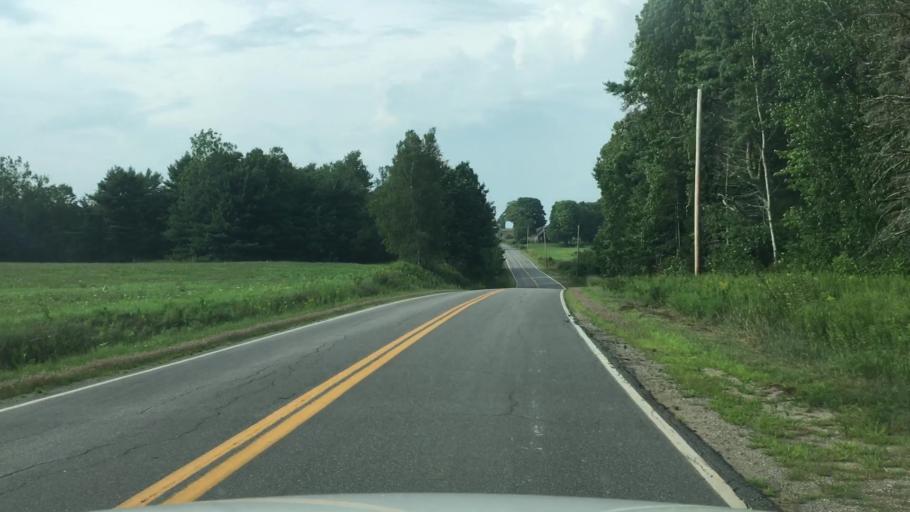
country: US
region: Maine
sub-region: Knox County
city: Washington
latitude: 44.2092
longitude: -69.3828
